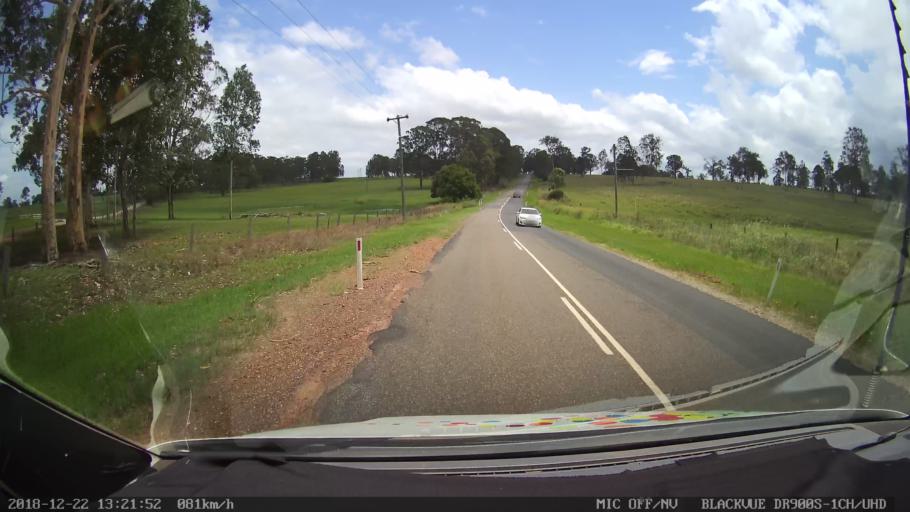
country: AU
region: New South Wales
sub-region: Clarence Valley
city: Coutts Crossing
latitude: -29.7813
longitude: 152.9164
